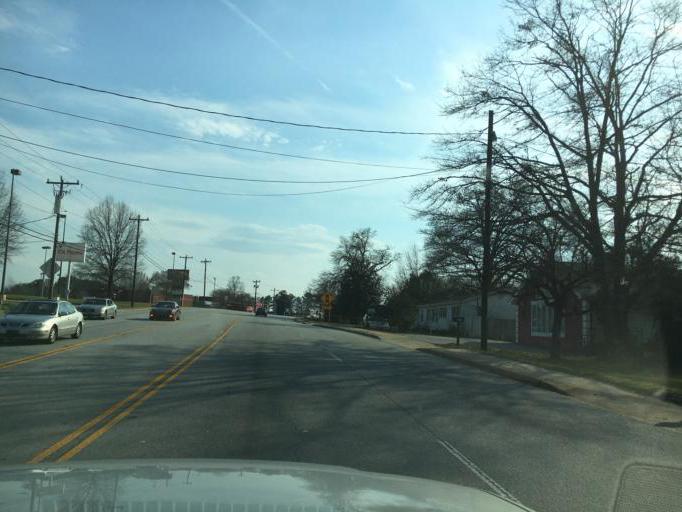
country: US
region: South Carolina
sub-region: Spartanburg County
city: Spartanburg
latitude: 34.9782
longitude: -81.9333
